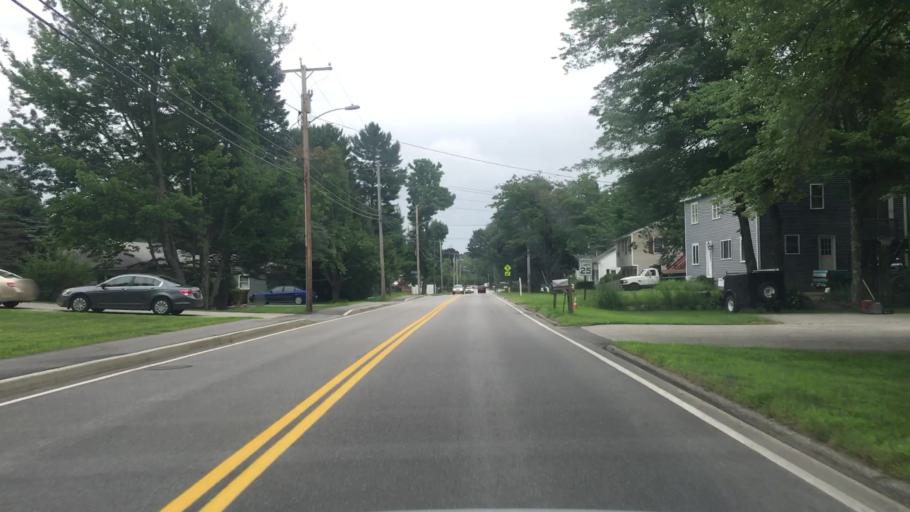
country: US
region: Maine
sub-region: York County
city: Biddeford
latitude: 43.5082
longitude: -70.4591
